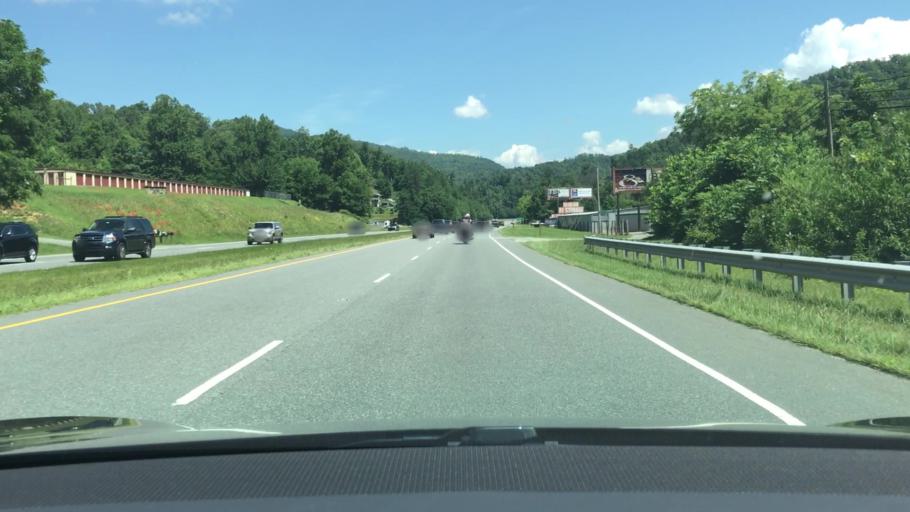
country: US
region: North Carolina
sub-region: Jackson County
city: Sylva
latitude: 35.3198
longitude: -83.2621
